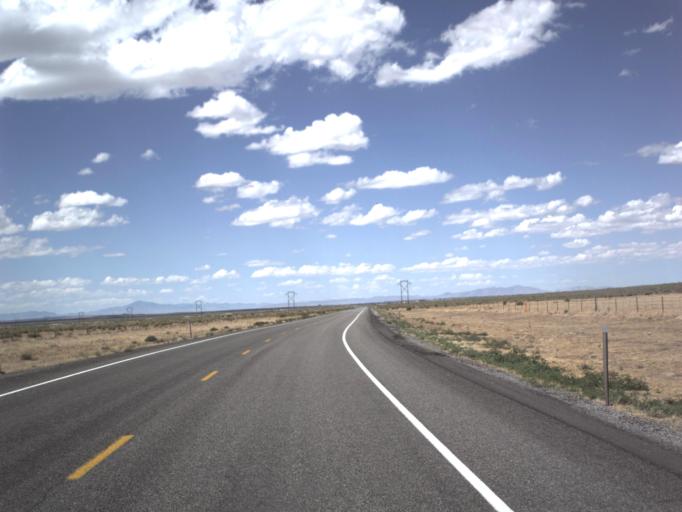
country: US
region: Utah
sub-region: Millard County
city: Fillmore
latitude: 39.1502
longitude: -112.3965
